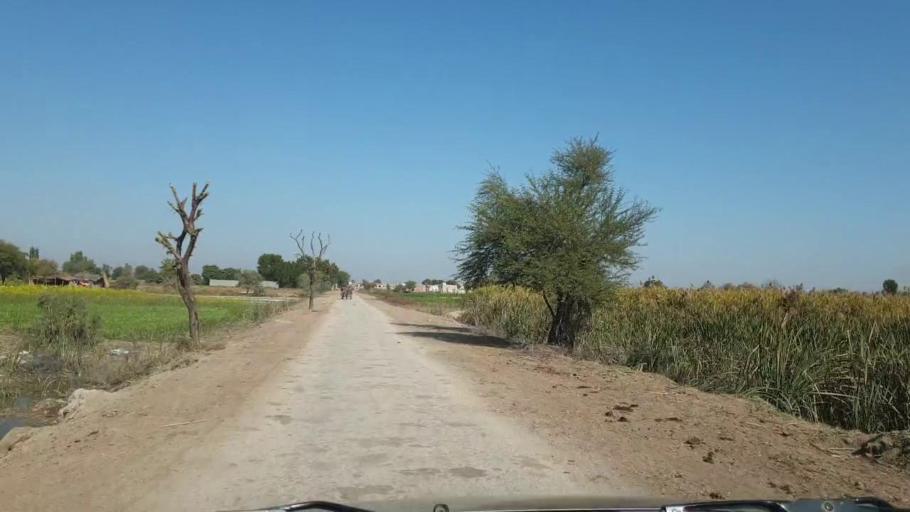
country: PK
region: Sindh
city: Sinjhoro
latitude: 26.1065
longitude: 68.8427
